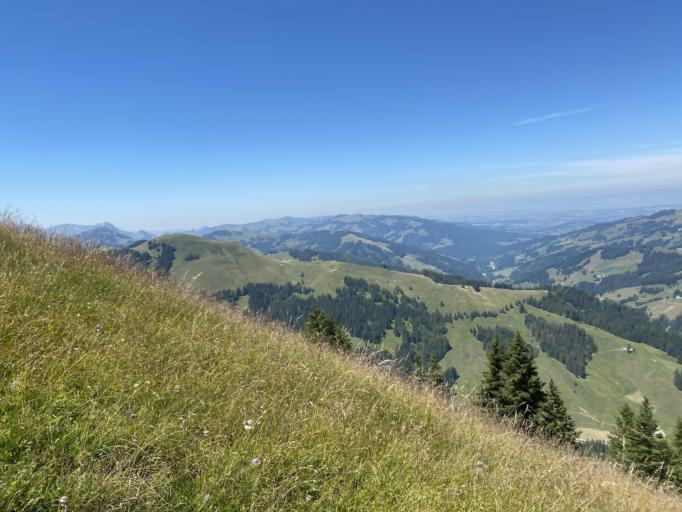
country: CH
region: Bern
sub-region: Bern-Mittelland District
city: Ruschegg
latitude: 46.7057
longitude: 7.4096
